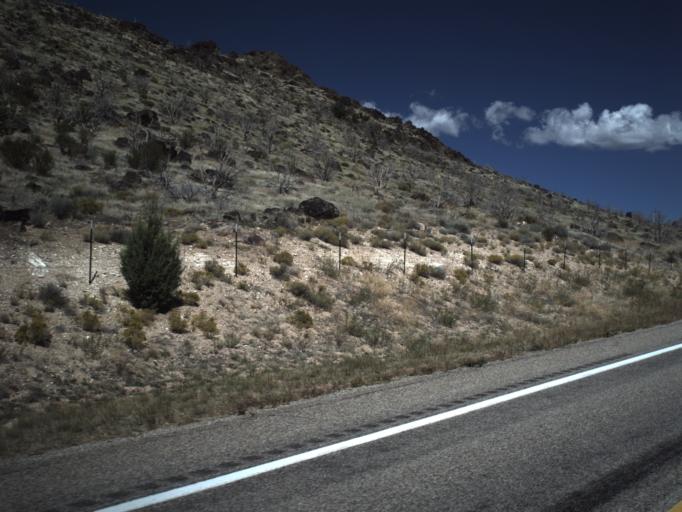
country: US
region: Utah
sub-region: Washington County
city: Ivins
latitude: 37.3732
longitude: -113.6587
